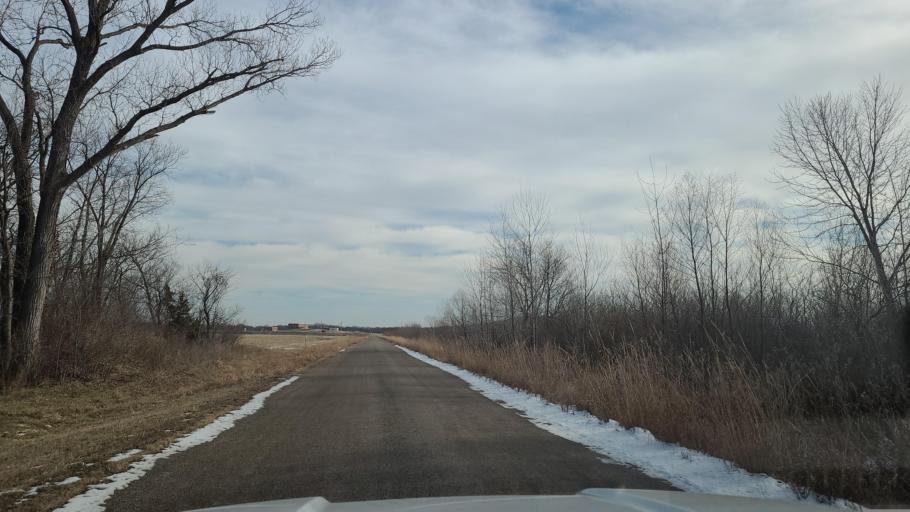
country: US
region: Kansas
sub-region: Douglas County
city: Lawrence
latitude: 38.9100
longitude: -95.2130
